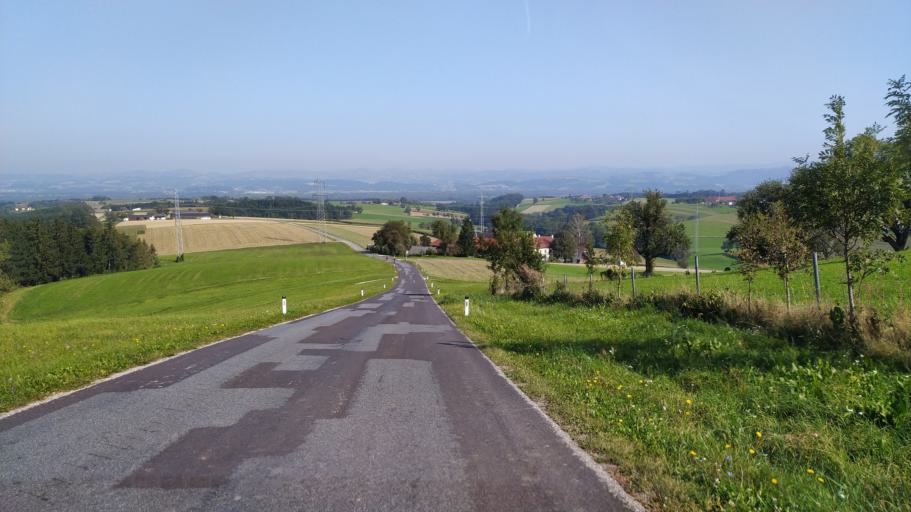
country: AT
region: Lower Austria
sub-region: Politischer Bezirk Amstetten
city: Zeillern
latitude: 48.1290
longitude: 14.7530
